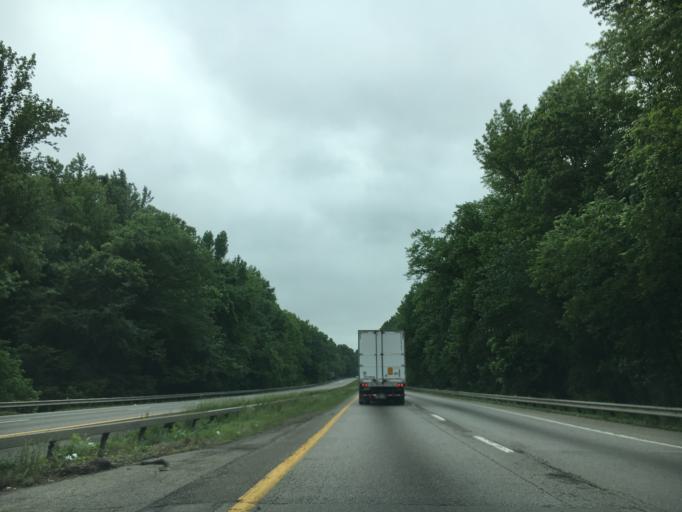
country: US
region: Virginia
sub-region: City of Petersburg
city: Petersburg
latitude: 37.2132
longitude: -77.3983
